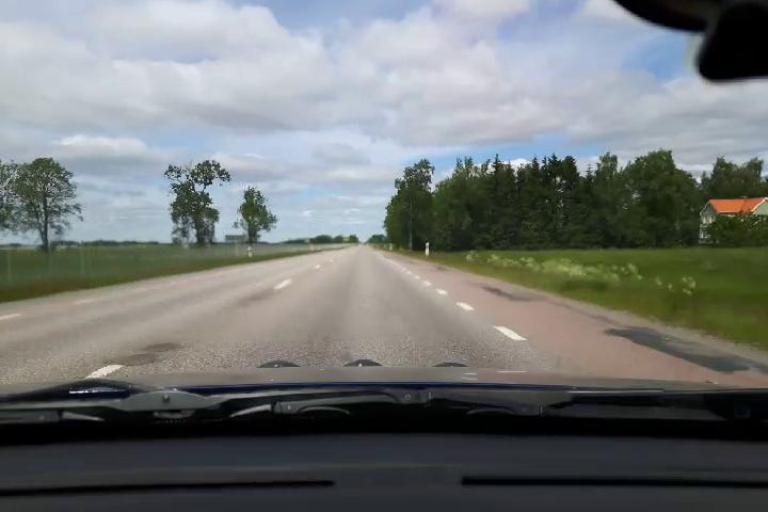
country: SE
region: Uppsala
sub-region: Uppsala Kommun
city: Gamla Uppsala
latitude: 59.8923
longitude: 17.6163
